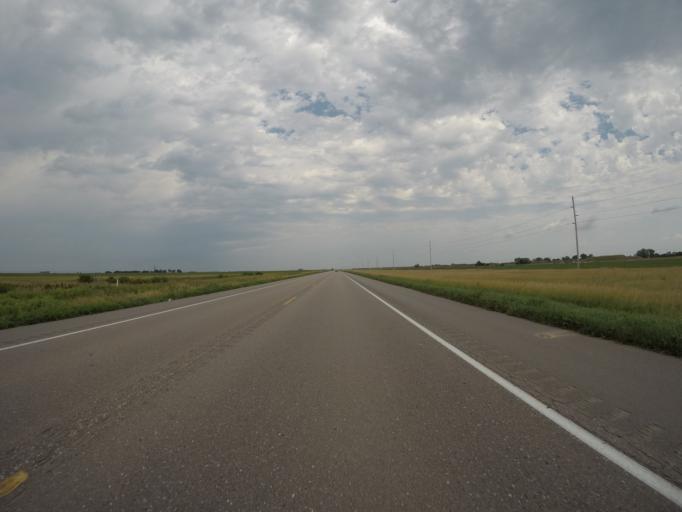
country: US
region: Nebraska
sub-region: Clay County
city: Harvard
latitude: 40.5824
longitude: -98.2133
